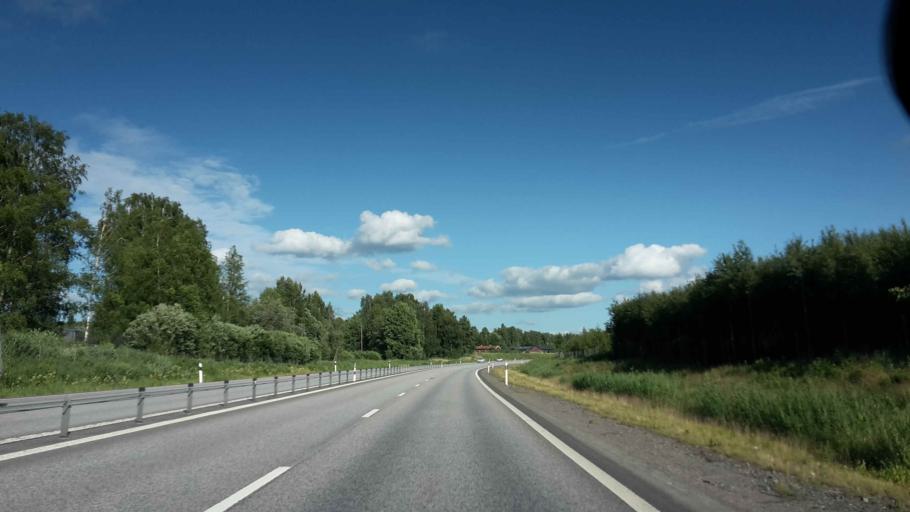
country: SE
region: OEstergoetland
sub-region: Norrkopings Kommun
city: Svartinge
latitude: 58.6446
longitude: 16.0778
